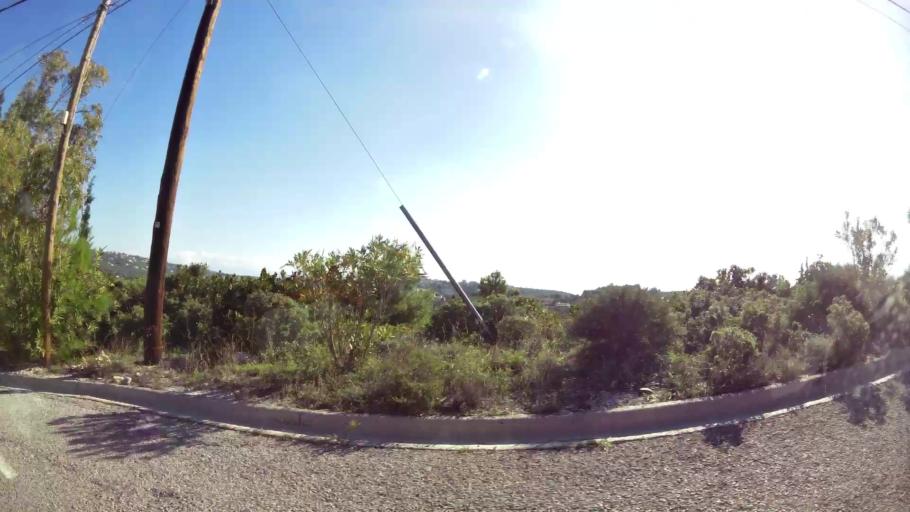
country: GR
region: Attica
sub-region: Nomarchia Anatolikis Attikis
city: Dhrafi
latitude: 38.0189
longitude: 23.9004
